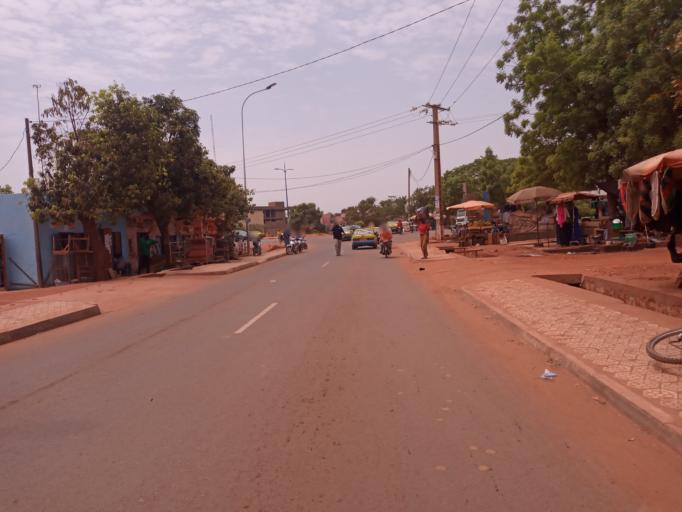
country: ML
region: Bamako
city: Bamako
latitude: 12.5802
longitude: -7.9882
